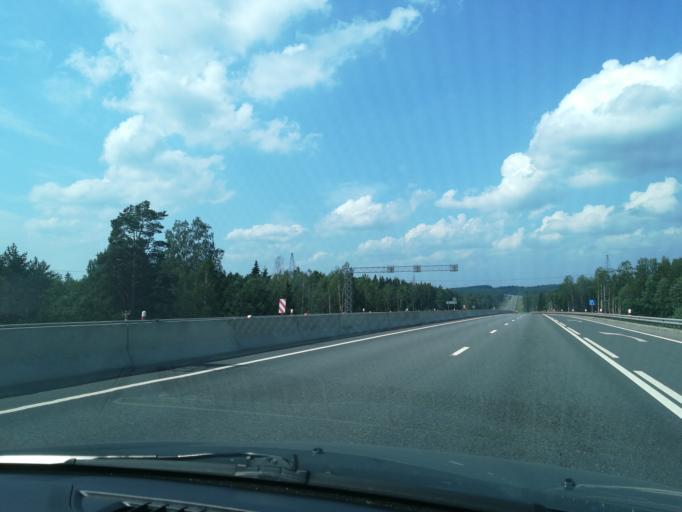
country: RU
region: Leningrad
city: Vistino
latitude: 59.6227
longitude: 28.6426
